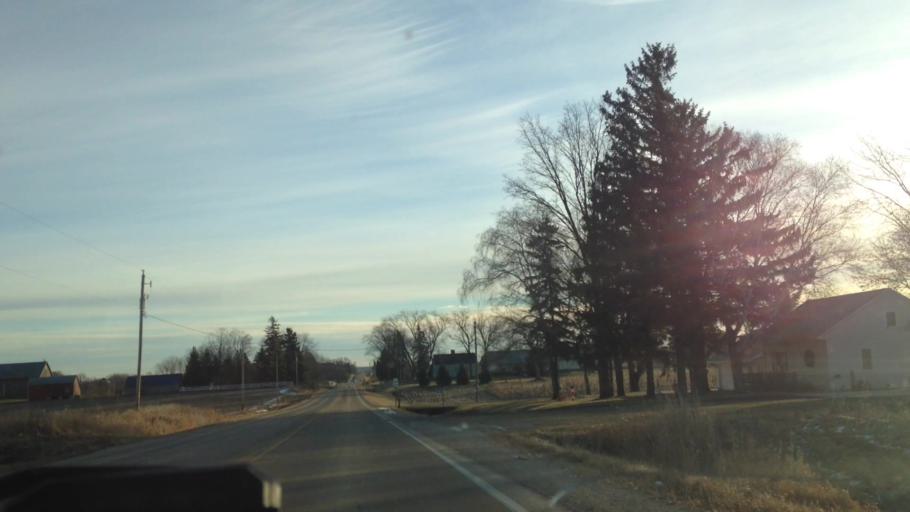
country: US
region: Wisconsin
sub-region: Dodge County
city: Theresa
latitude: 43.5366
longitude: -88.4861
